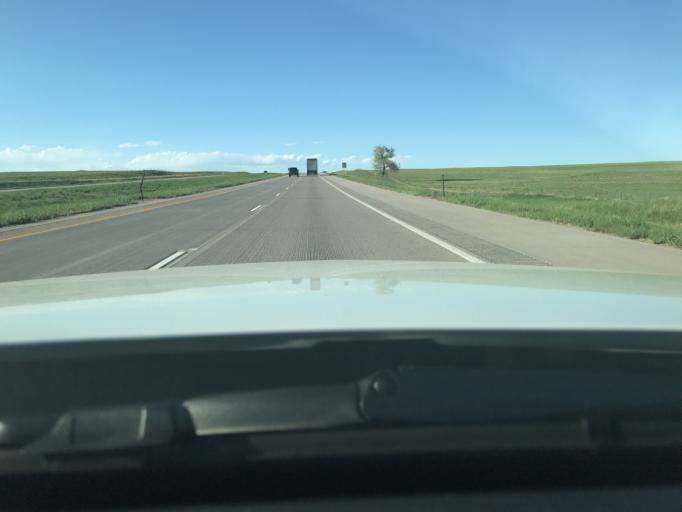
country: US
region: Colorado
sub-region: Larimer County
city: Wellington
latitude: 40.8502
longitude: -104.9630
